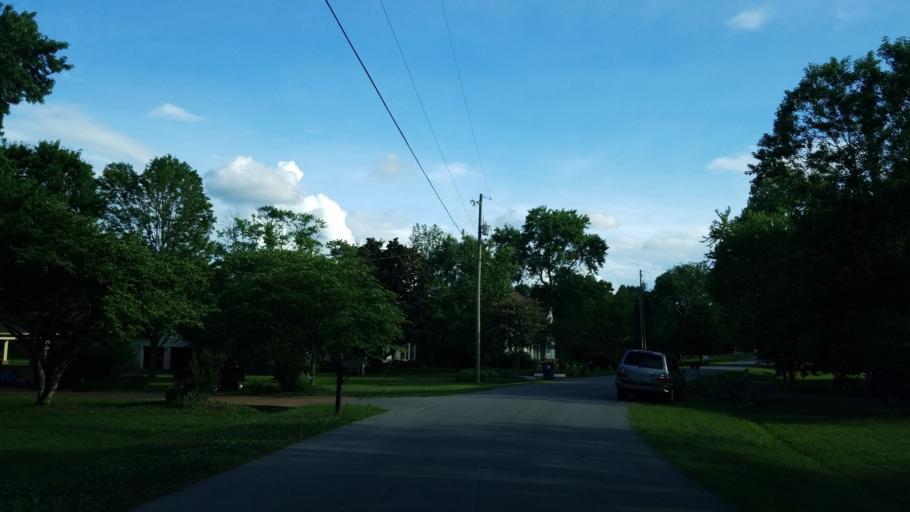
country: US
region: Tennessee
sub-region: Williamson County
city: Brentwood
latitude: 36.0296
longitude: -86.8031
